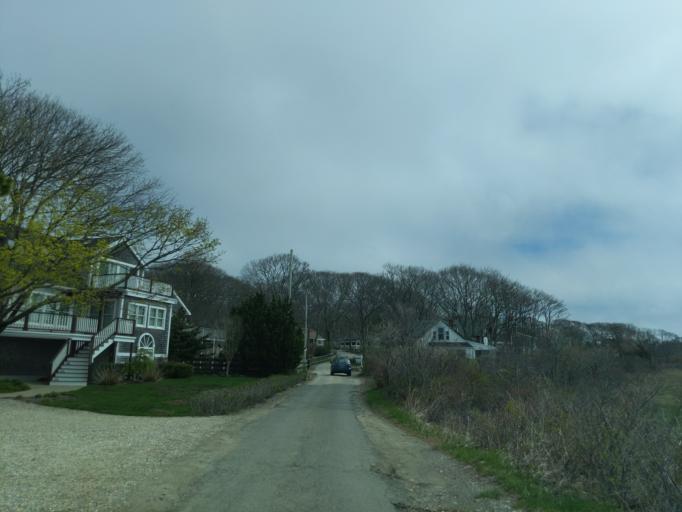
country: US
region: Massachusetts
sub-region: Essex County
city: Rockport
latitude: 42.6348
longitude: -70.6095
